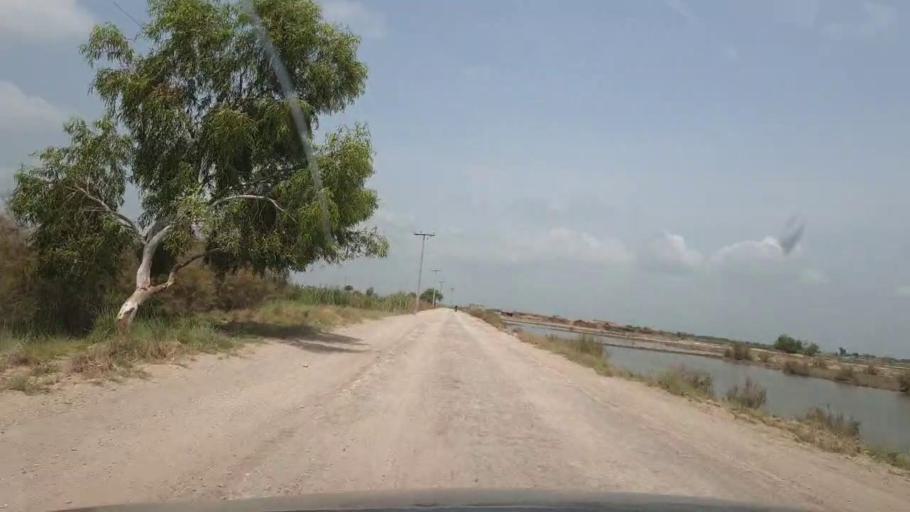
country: PK
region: Sindh
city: Ratodero
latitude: 27.9073
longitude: 68.3110
